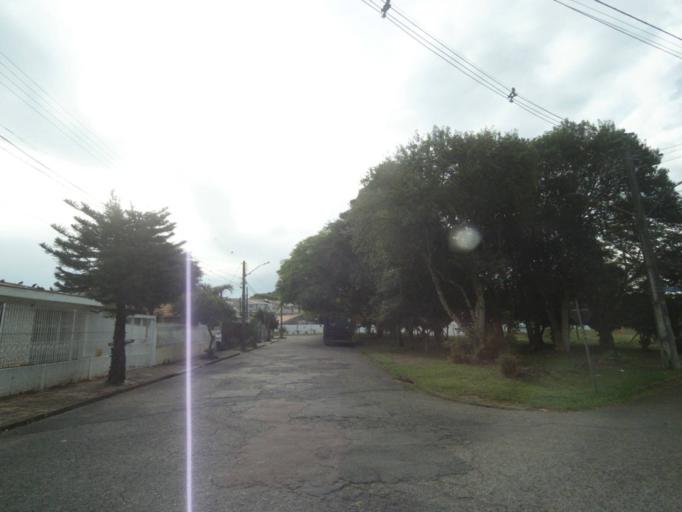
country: BR
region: Parana
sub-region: Curitiba
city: Curitiba
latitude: -25.4295
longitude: -49.2340
